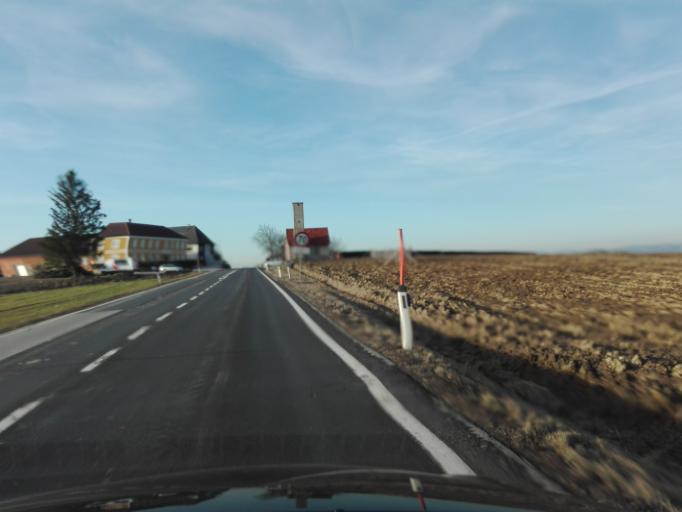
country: AT
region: Lower Austria
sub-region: Politischer Bezirk Amstetten
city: Strengberg
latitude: 48.1569
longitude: 14.6201
